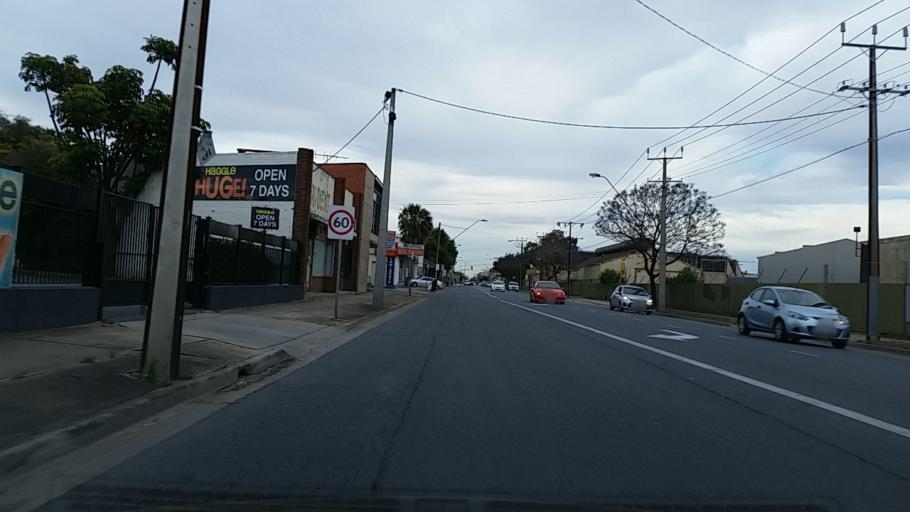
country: AU
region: South Australia
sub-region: Charles Sturt
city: Woodville
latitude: -34.8885
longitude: 138.5484
